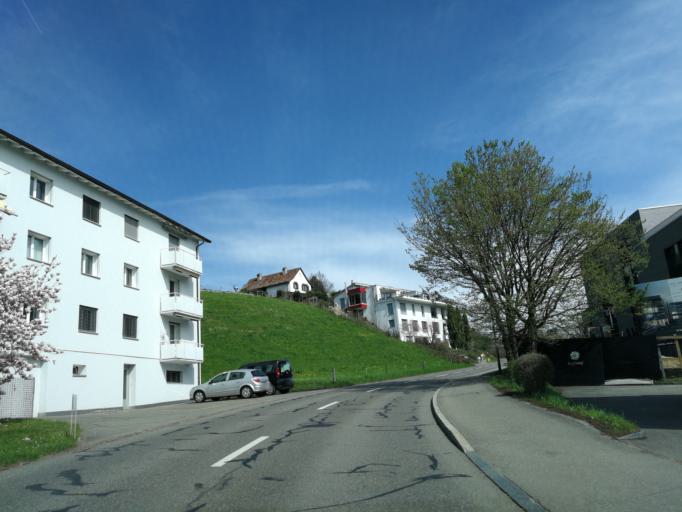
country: CH
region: Zurich
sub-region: Bezirk Meilen
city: Uetikon
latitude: 47.2610
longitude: 8.6834
